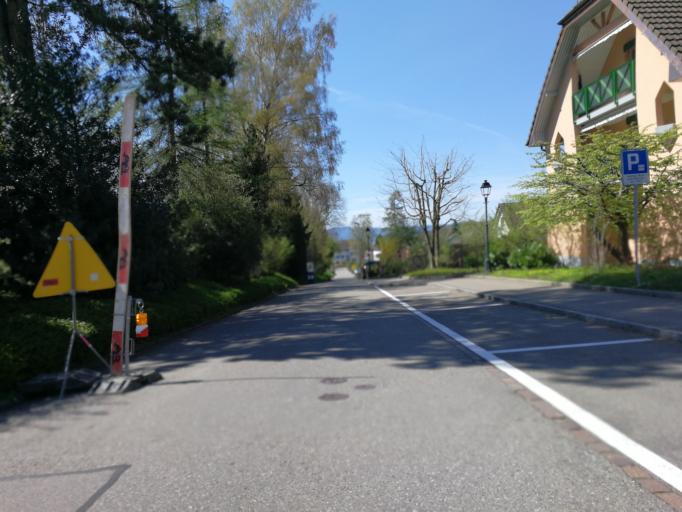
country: CH
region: Zurich
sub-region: Bezirk Meilen
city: Uetikon
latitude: 47.2625
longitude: 8.6769
